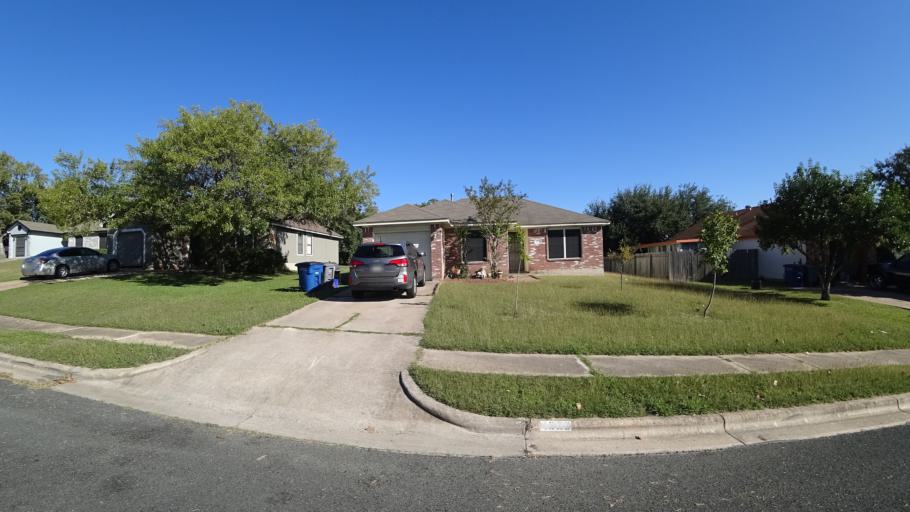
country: US
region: Texas
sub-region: Travis County
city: Austin
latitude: 30.2919
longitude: -97.6761
